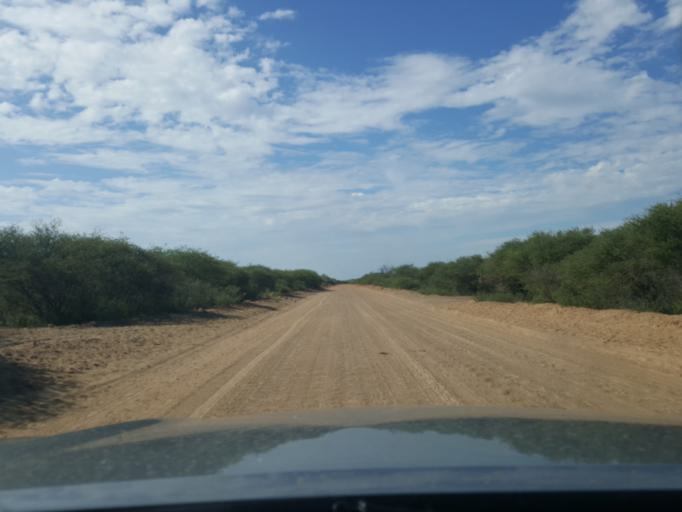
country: BW
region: Kweneng
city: Khudumelapye
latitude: -23.6498
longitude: 24.7274
